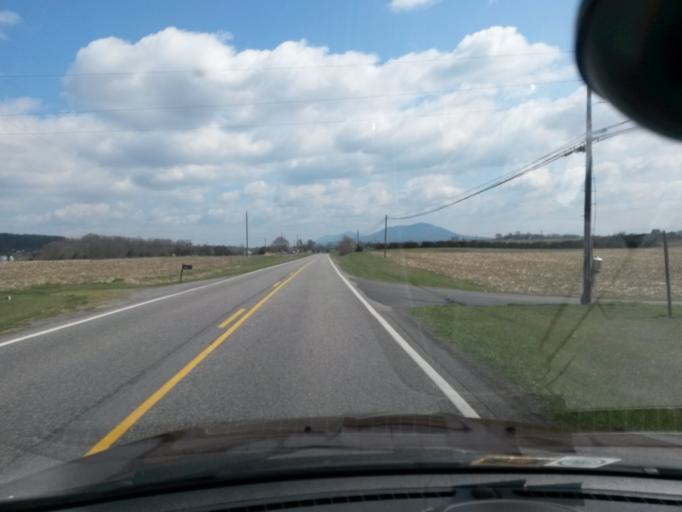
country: US
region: Virginia
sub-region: Augusta County
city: Weyers Cave
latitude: 38.3223
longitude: -78.8760
